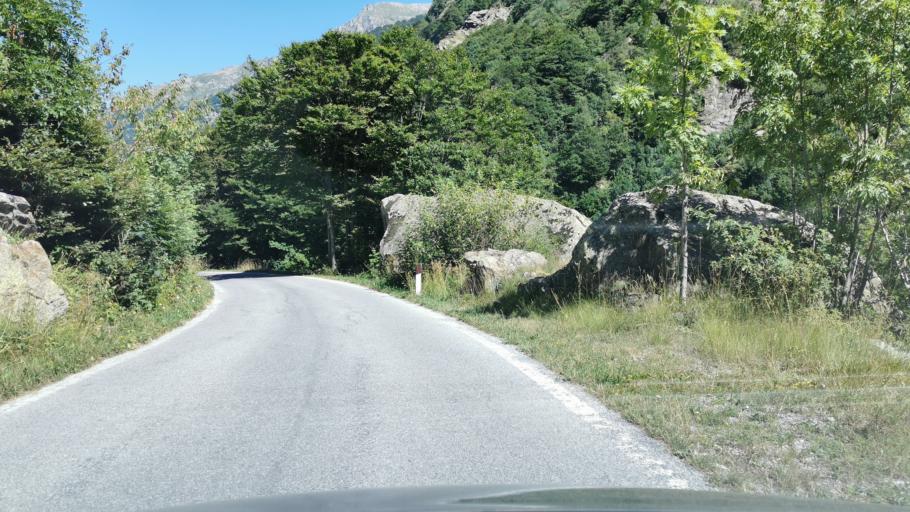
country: IT
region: Piedmont
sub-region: Provincia di Cuneo
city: Demonte
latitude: 44.2198
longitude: 7.2870
